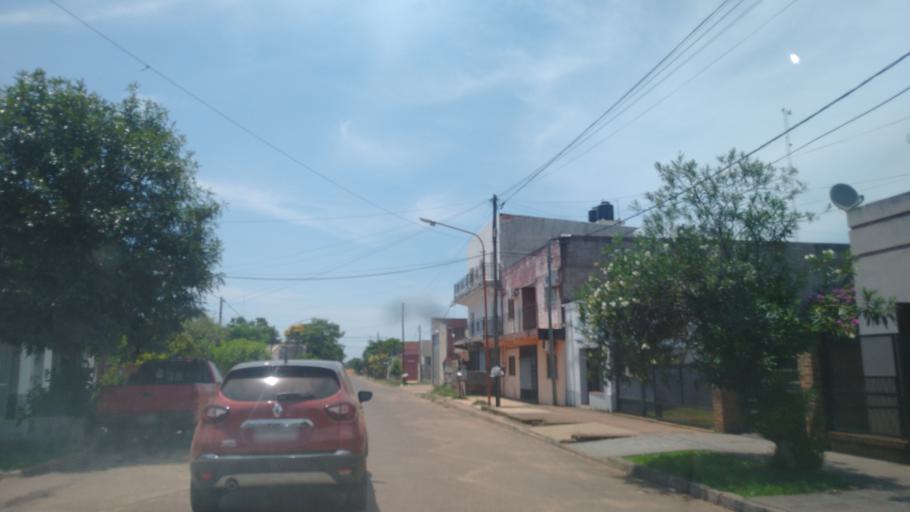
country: AR
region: Corrientes
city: Santo Tome
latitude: -28.5517
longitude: -56.0391
